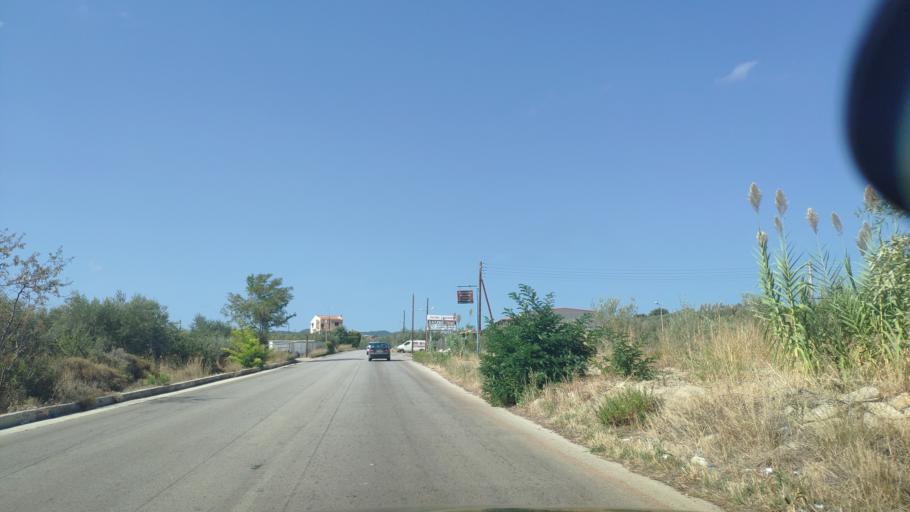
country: GR
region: Peloponnese
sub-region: Nomos Korinthias
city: Moulki
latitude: 37.9965
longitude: 22.7062
